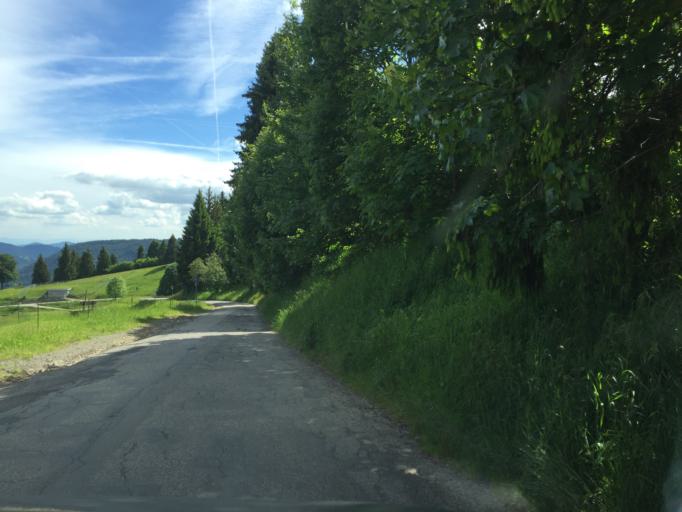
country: DE
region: Baden-Wuerttemberg
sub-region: Freiburg Region
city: Todtnau
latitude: 47.8580
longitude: 7.9411
